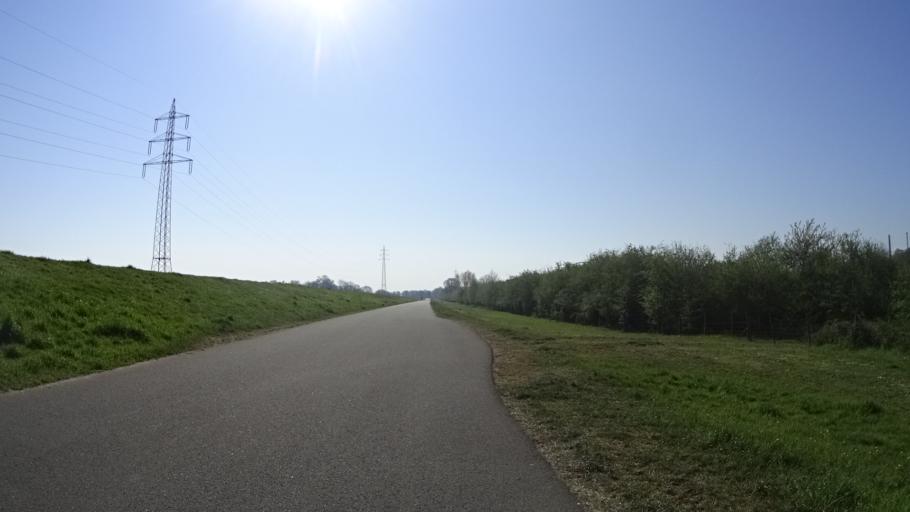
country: DE
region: North Rhine-Westphalia
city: Rheinberg
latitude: 51.5766
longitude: 6.5823
